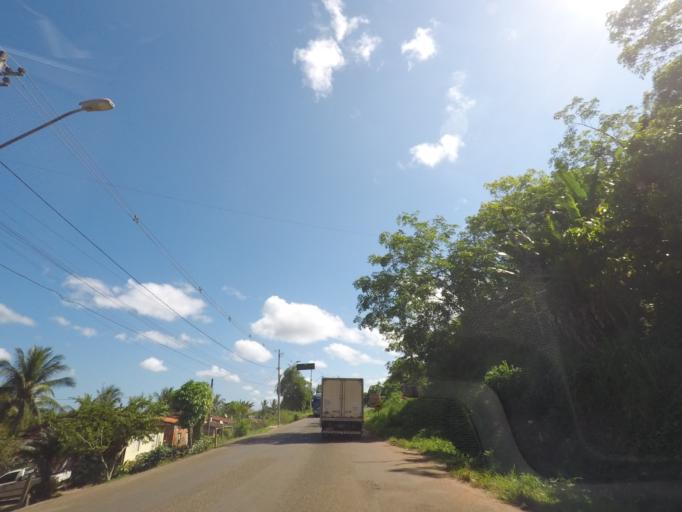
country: BR
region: Bahia
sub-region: Itubera
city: Itubera
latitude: -13.7495
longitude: -39.1530
